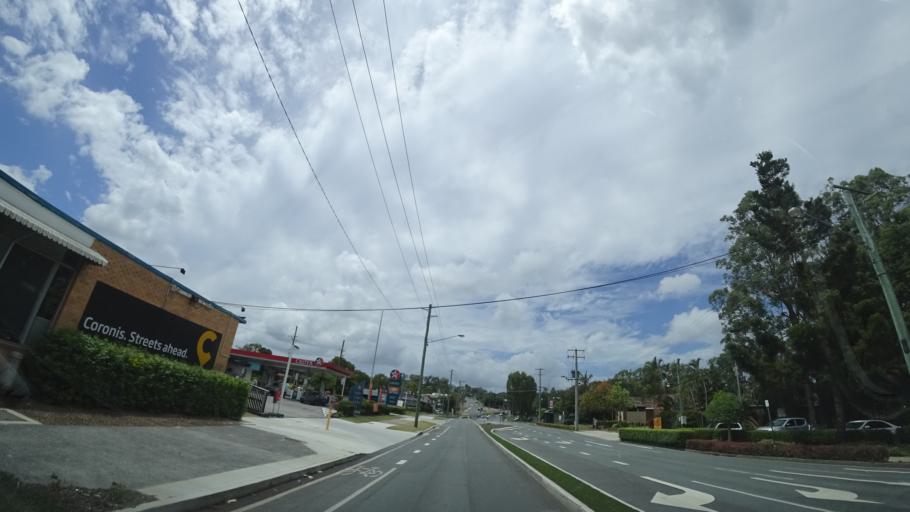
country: AU
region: Queensland
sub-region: Moreton Bay
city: Ferny Hills
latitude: -27.3974
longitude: 152.9610
